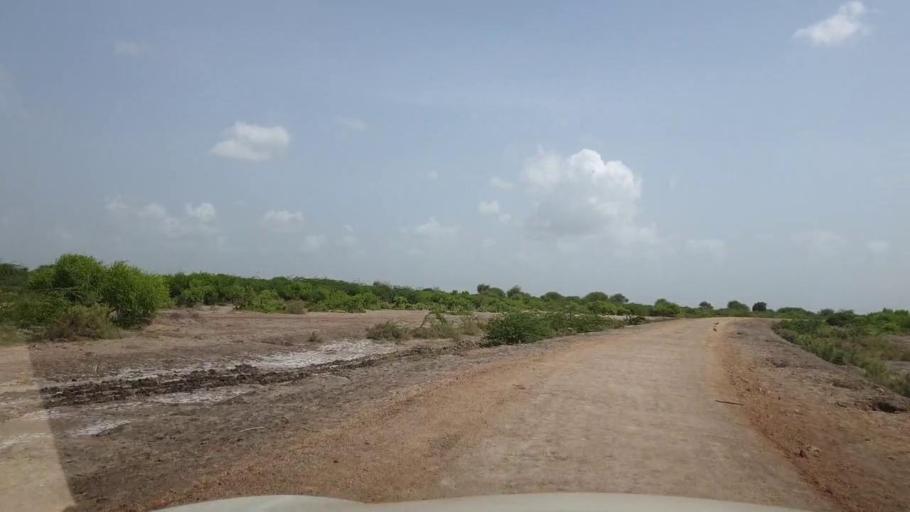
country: PK
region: Sindh
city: Kadhan
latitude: 24.3923
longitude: 68.7946
